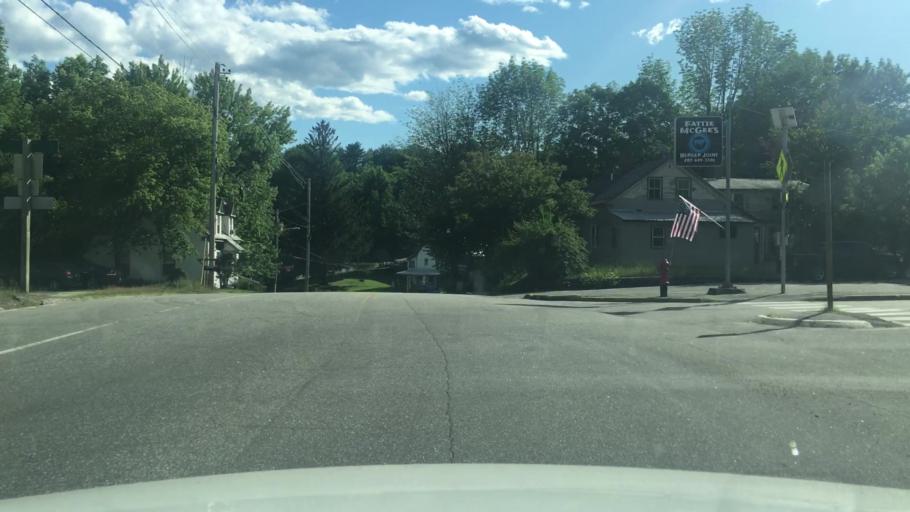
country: US
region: Maine
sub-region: Franklin County
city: Wilton
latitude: 44.5928
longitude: -70.2281
